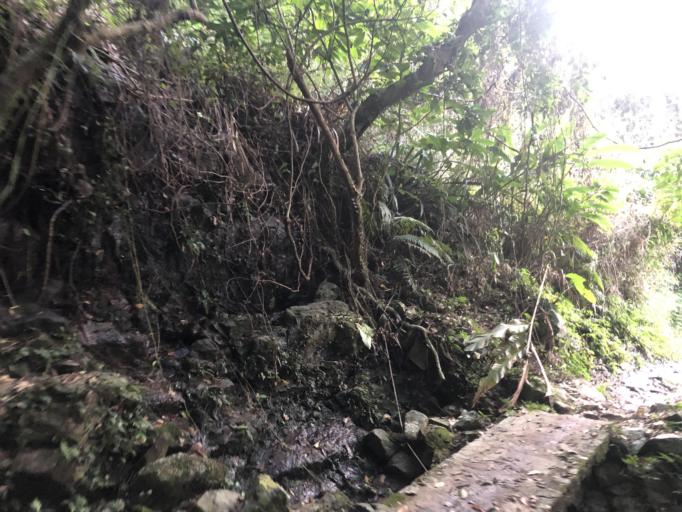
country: HK
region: Tsuen Wan
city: Tsuen Wan
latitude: 22.3994
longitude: 114.0794
